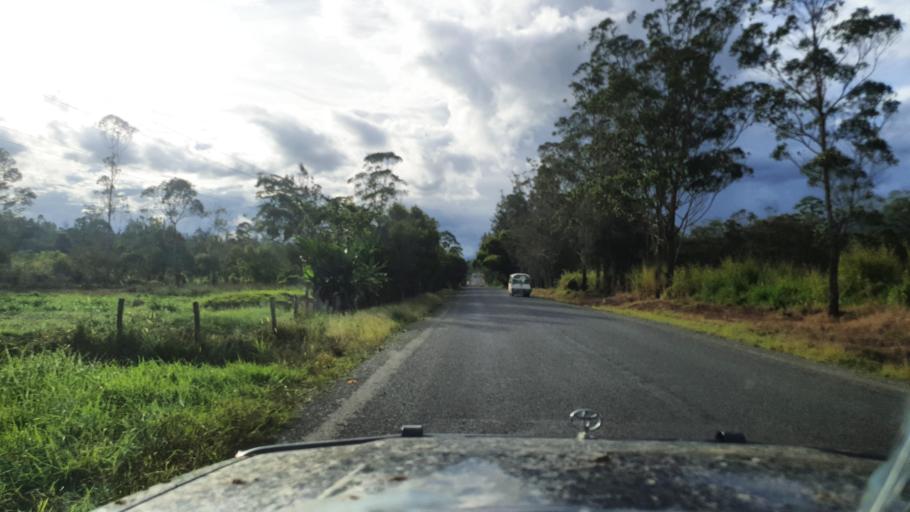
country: PG
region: Jiwaka
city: Minj
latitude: -5.8230
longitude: 144.4972
